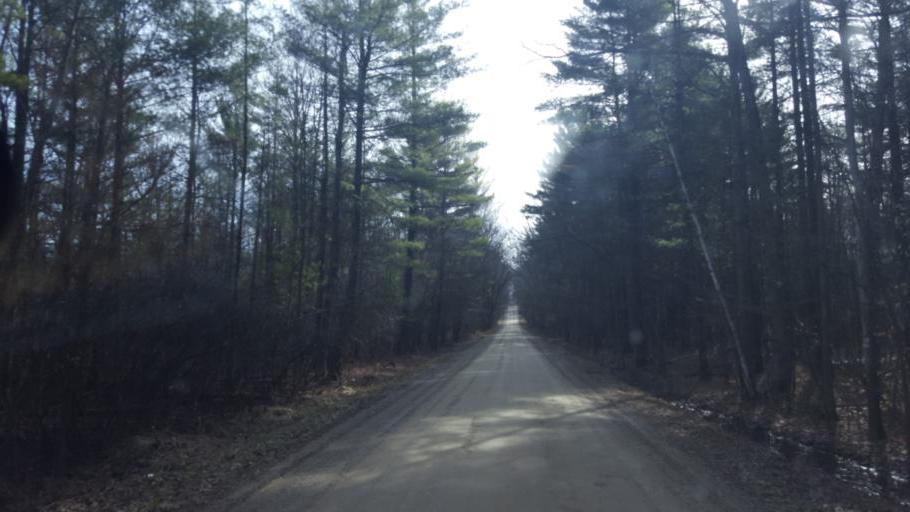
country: US
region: Michigan
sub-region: Montcalm County
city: Howard City
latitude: 43.5403
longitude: -85.5587
